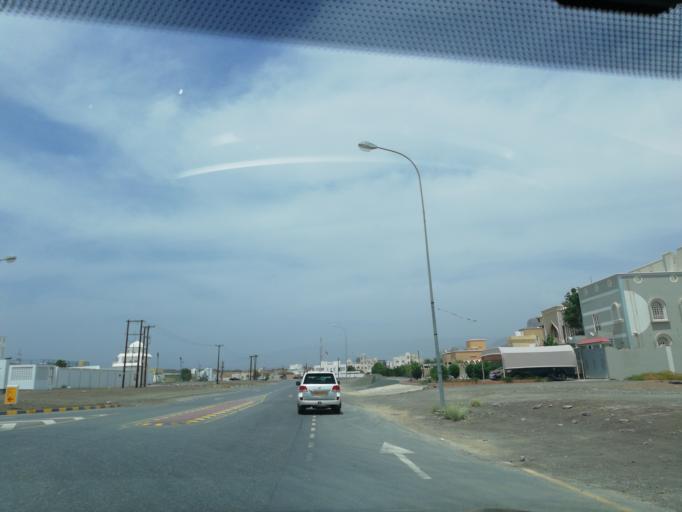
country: OM
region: Muhafazat ad Dakhiliyah
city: Nizwa
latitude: 22.8592
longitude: 57.5197
